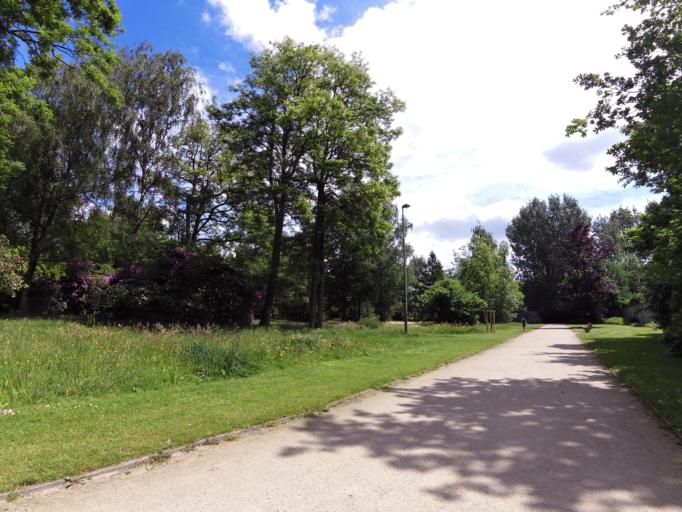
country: BE
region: Flanders
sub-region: Provincie Oost-Vlaanderen
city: Ledeberg
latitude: 51.0648
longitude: 3.7549
